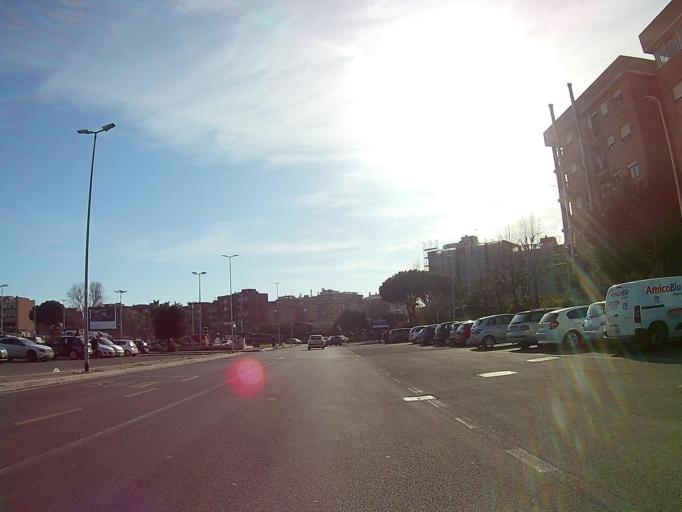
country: IT
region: Latium
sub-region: Citta metropolitana di Roma Capitale
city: Lido di Ostia
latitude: 41.7386
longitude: 12.2619
